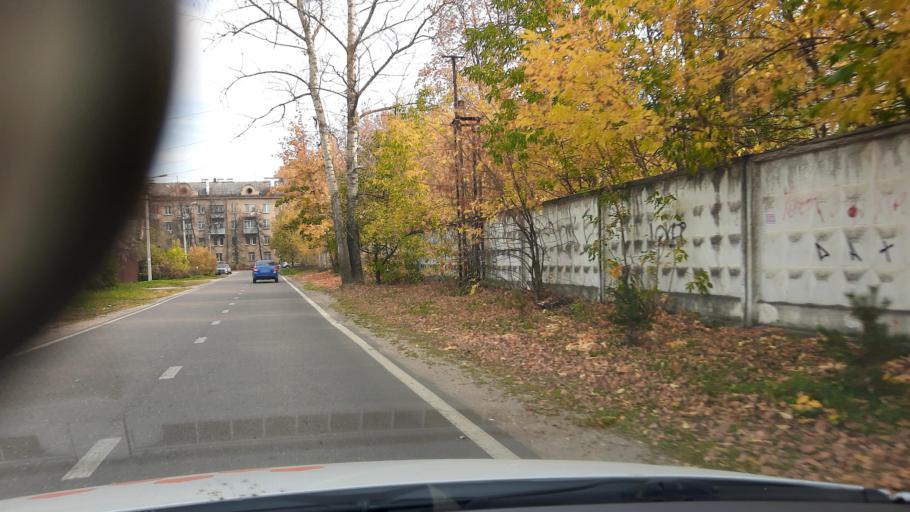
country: RU
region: Moskovskaya
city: Elektrostal'
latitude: 55.7956
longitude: 38.4340
